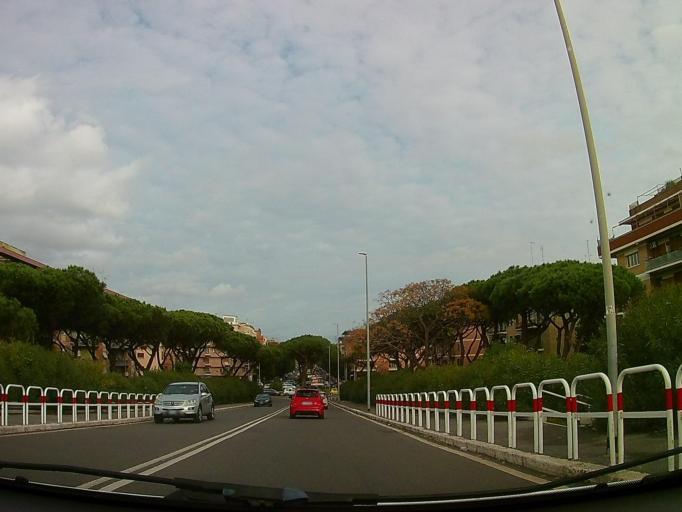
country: IT
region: Latium
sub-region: Citta metropolitana di Roma Capitale
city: Lido di Ostia
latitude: 41.7311
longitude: 12.2892
